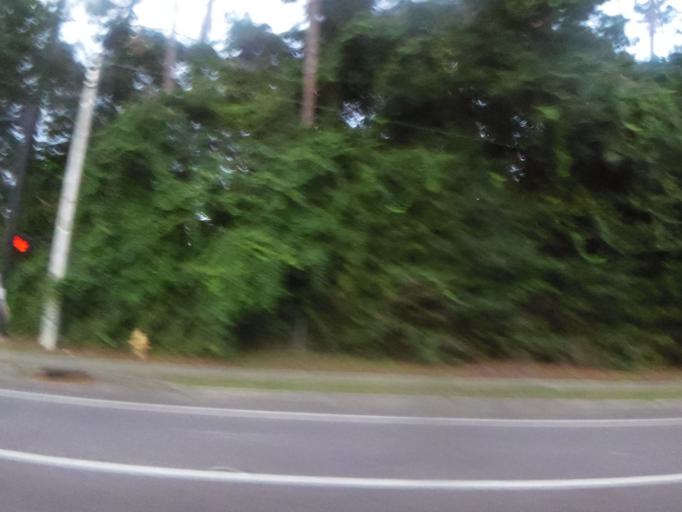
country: US
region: Florida
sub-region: Duval County
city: Jacksonville
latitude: 30.2413
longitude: -81.6084
